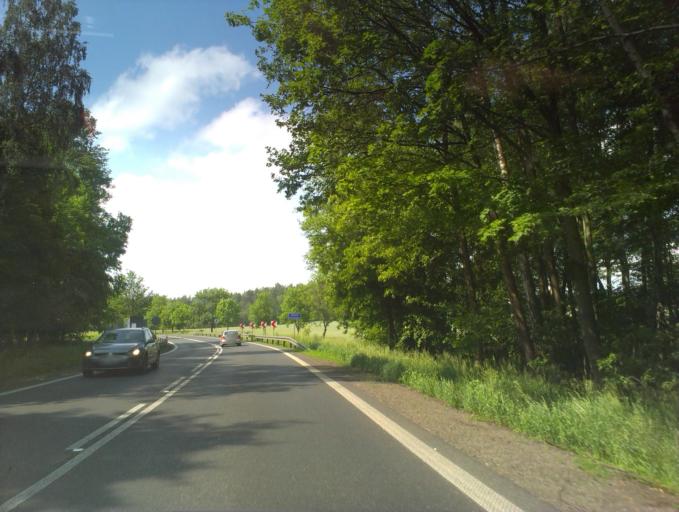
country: PL
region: Greater Poland Voivodeship
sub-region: Powiat zlotowski
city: Jastrowie
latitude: 53.4608
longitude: 16.8538
